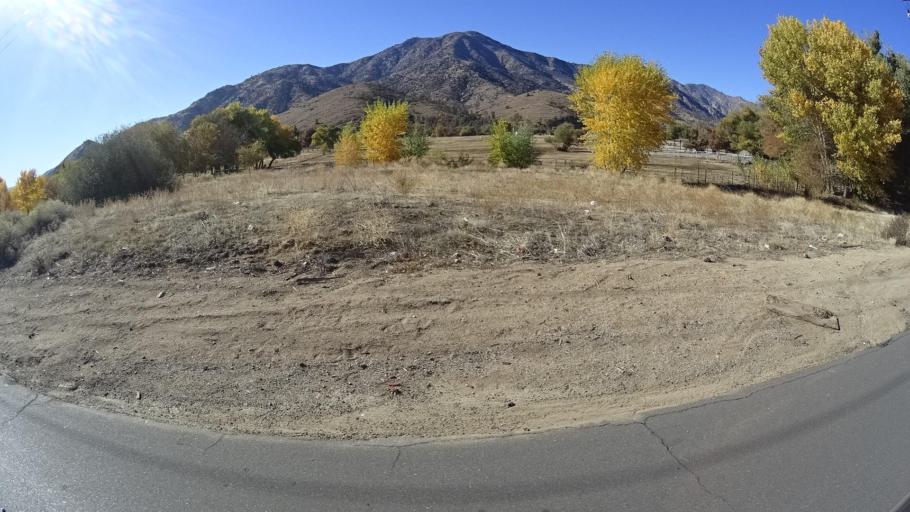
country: US
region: California
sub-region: Kern County
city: Kernville
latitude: 35.7484
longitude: -118.4137
